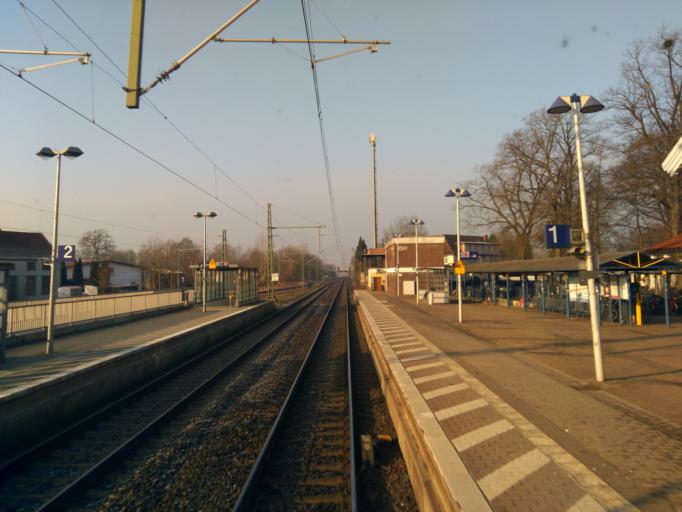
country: DE
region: Lower Saxony
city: Ottersberg
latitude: 53.0969
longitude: 9.1325
